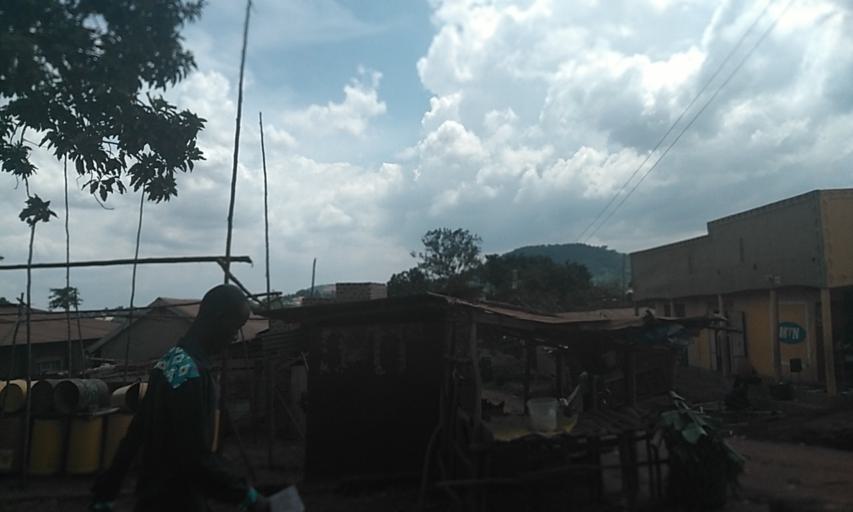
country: UG
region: Central Region
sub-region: Wakiso District
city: Wakiso
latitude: 0.3998
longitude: 32.4839
